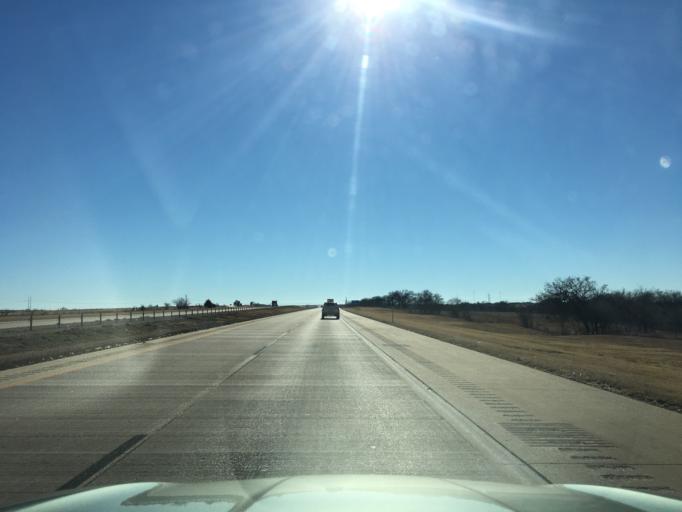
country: US
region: Oklahoma
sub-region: Noble County
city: Perry
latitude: 36.4331
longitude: -97.3271
